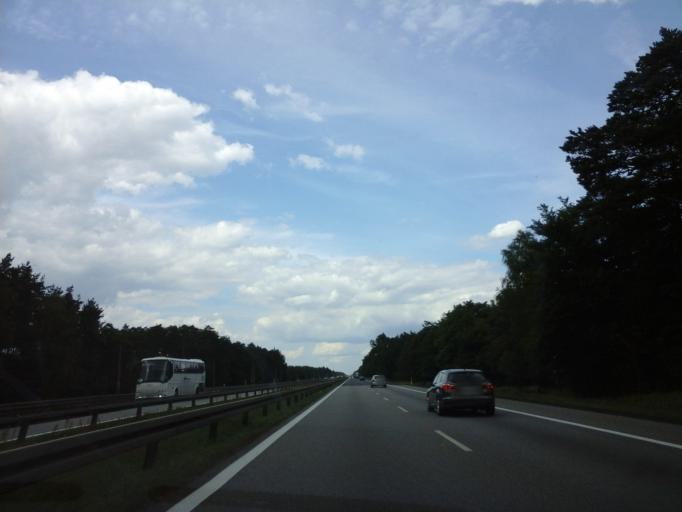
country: PL
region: West Pomeranian Voivodeship
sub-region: Powiat goleniowski
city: Goleniow
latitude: 53.4730
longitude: 14.7889
